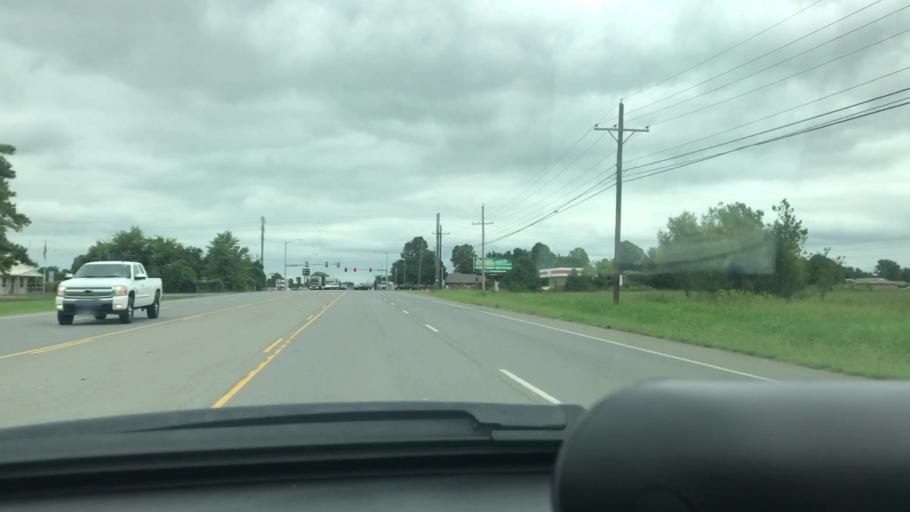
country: US
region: Oklahoma
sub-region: Wagoner County
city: Wagoner
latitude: 35.9423
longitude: -95.3952
